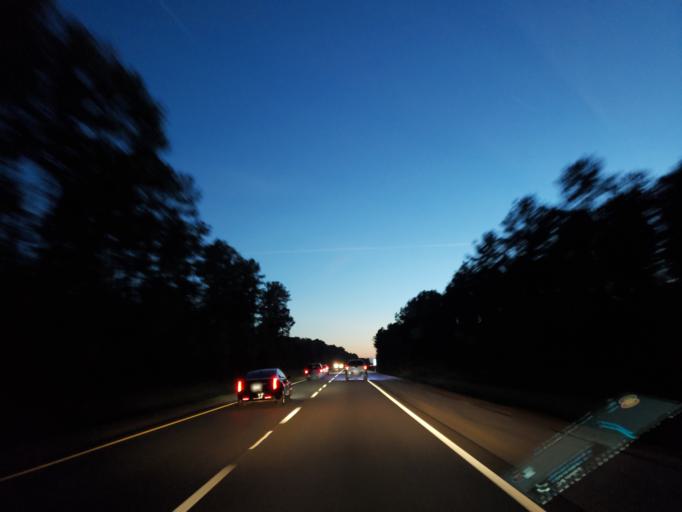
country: US
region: Mississippi
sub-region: Clarke County
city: Stonewall
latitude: 32.2512
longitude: -88.8249
